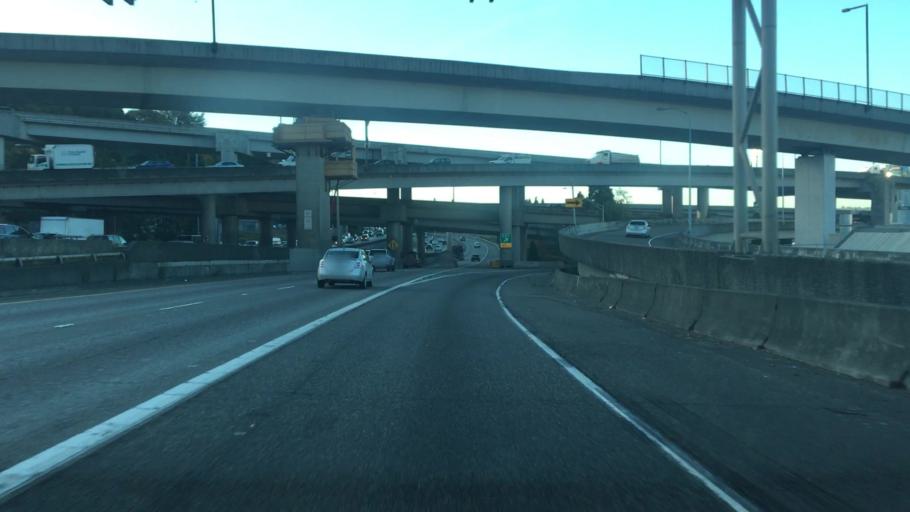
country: US
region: Washington
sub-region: King County
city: Seattle
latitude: 47.5947
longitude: -122.3210
